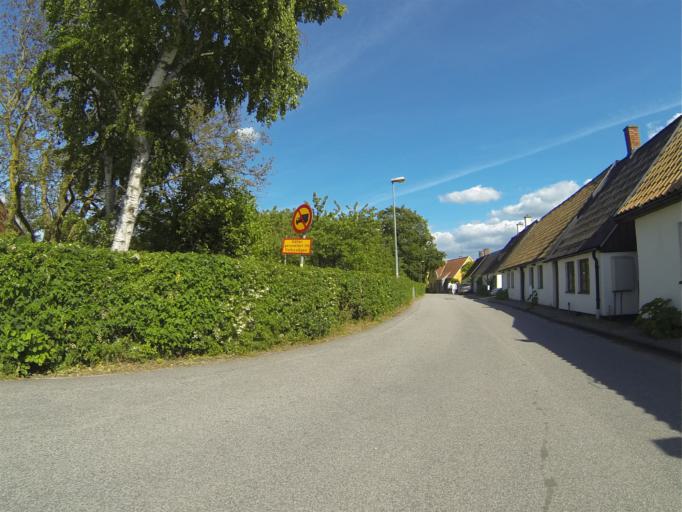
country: SE
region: Skane
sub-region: Lunds Kommun
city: Lund
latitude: 55.6859
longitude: 13.2222
